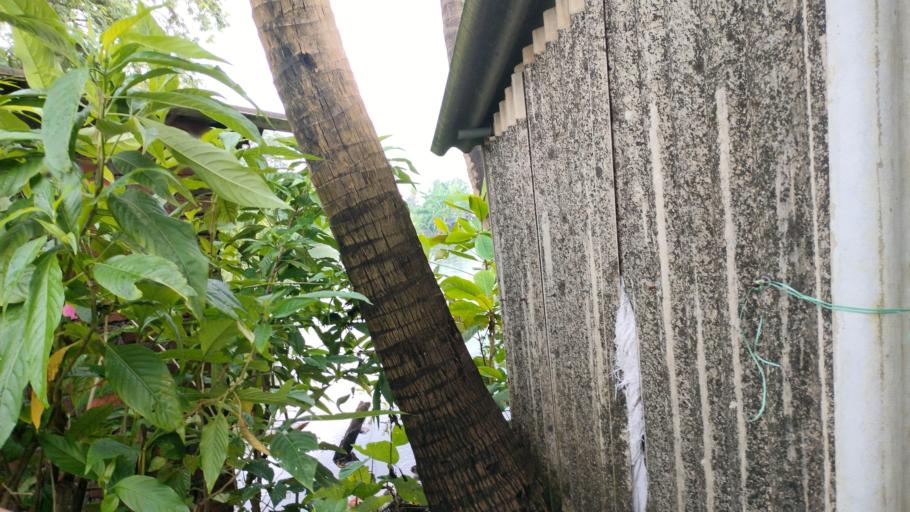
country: IN
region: Maharashtra
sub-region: Thane
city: Virar
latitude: 19.4075
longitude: 72.8054
